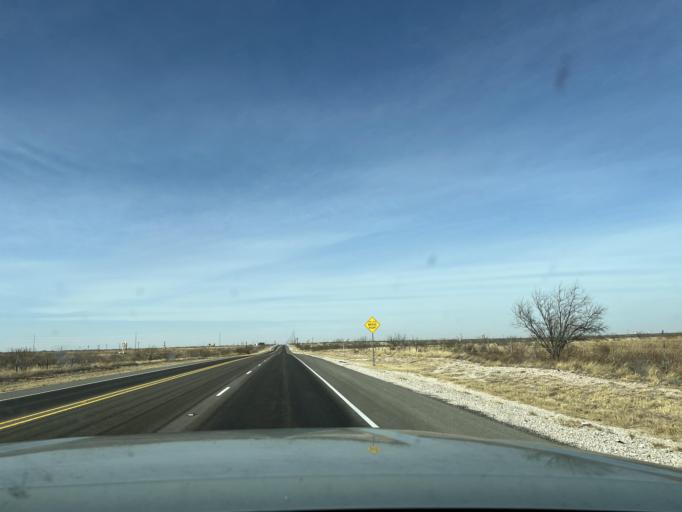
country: US
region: Texas
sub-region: Andrews County
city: Andrews
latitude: 32.3314
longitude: -102.6463
